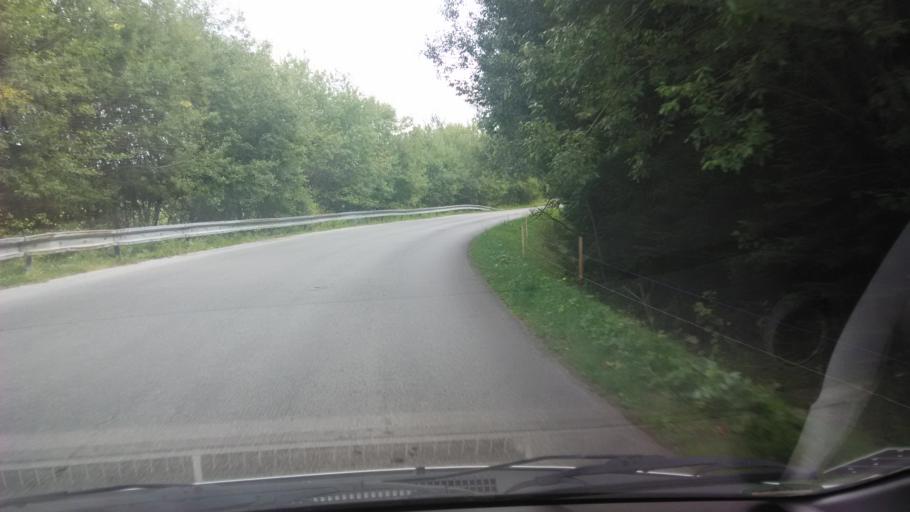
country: SK
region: Banskobystricky
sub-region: Okres Ziar nad Hronom
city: Kremnica
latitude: 48.7434
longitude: 18.9168
